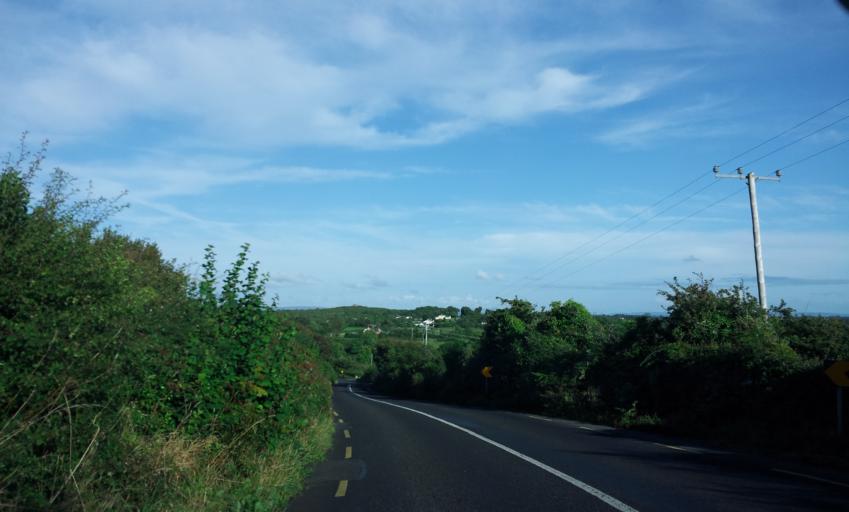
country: IE
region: Munster
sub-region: An Clar
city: Ennis
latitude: 52.9774
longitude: -9.1114
